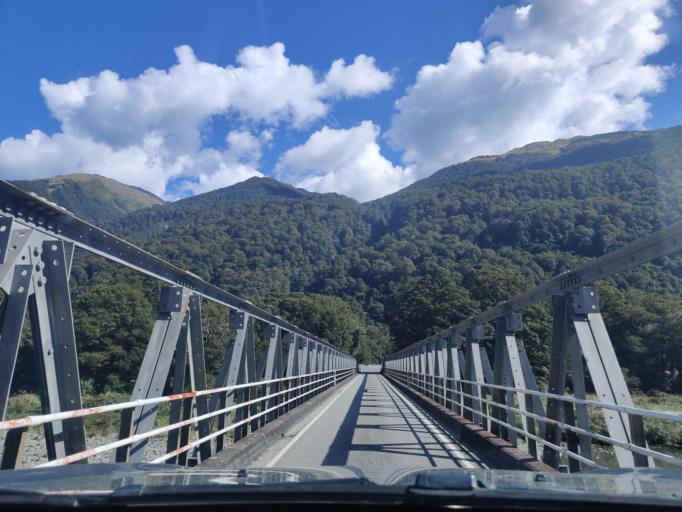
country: NZ
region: Otago
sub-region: Queenstown-Lakes District
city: Wanaka
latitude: -44.0126
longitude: 169.3839
